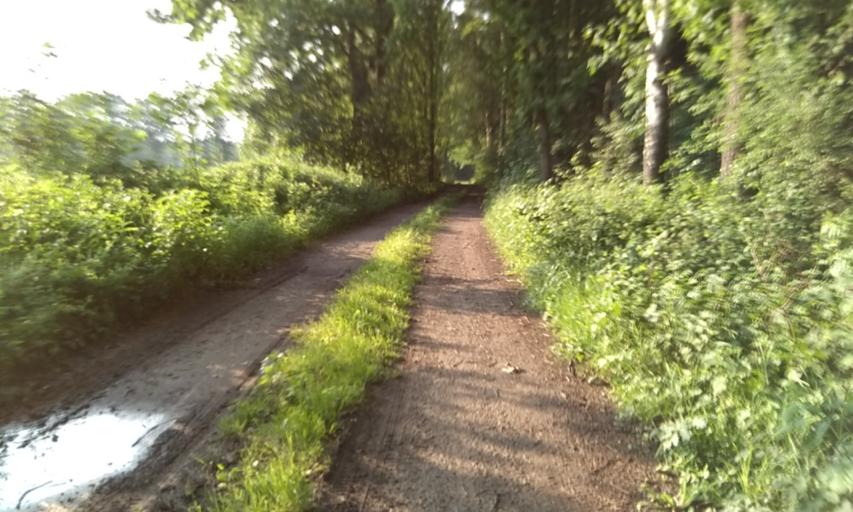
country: DE
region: Lower Saxony
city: Beckdorf
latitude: 53.4247
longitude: 9.5742
